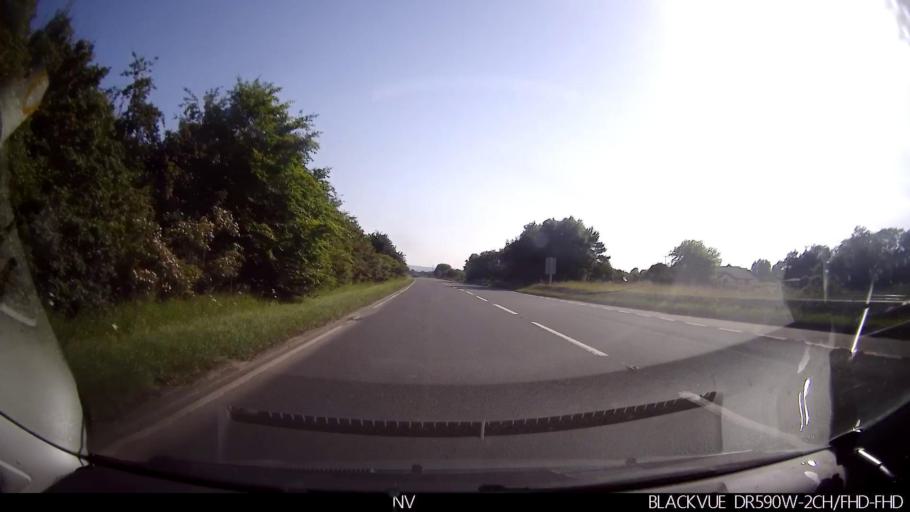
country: GB
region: England
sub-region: North Yorkshire
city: East Ayton
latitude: 54.2297
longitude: -0.4301
